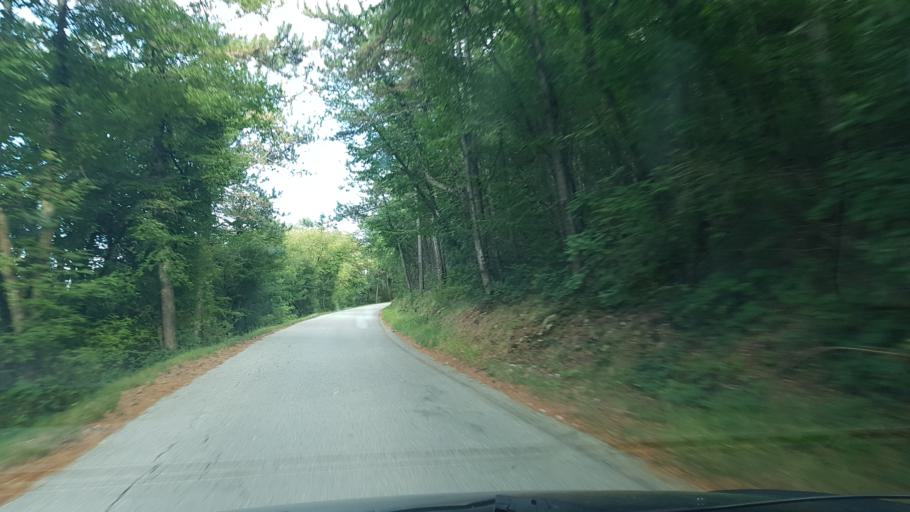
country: SI
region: Rence-Vogrsko
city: Rence
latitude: 45.8692
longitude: 13.6582
